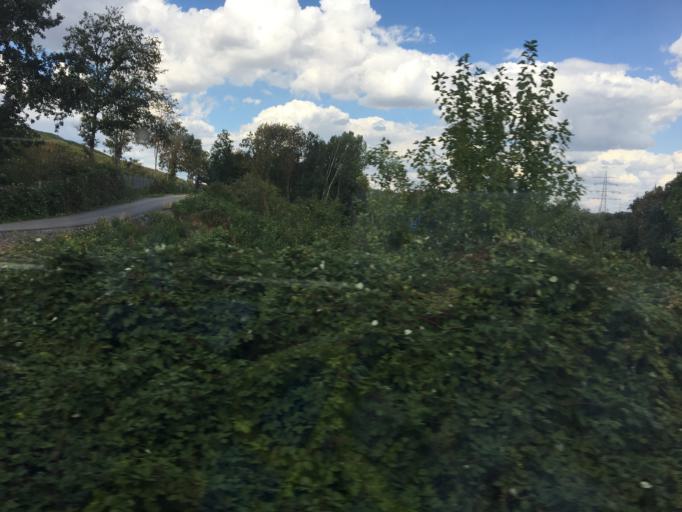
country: DE
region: North Rhine-Westphalia
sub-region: Regierungsbezirk Arnsberg
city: Bochum
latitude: 51.4818
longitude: 7.2782
